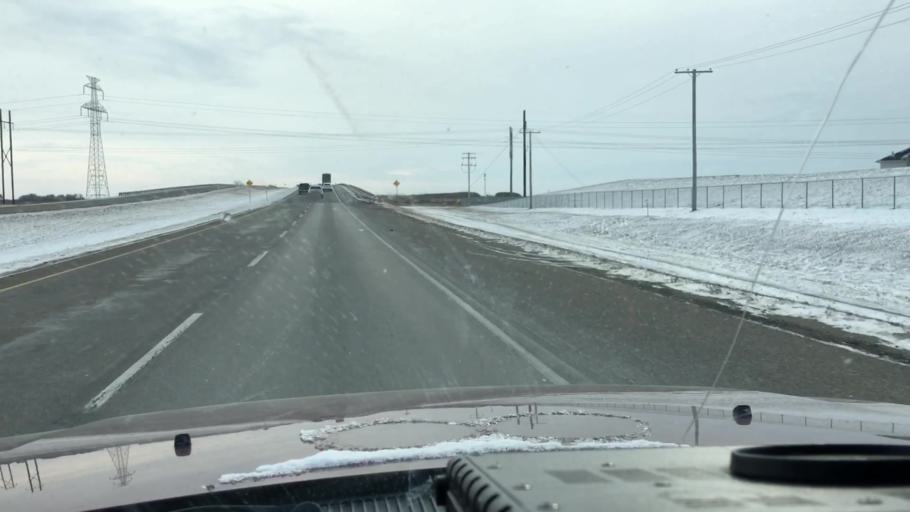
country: CA
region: Saskatchewan
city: Saskatoon
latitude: 52.0736
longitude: -106.6044
